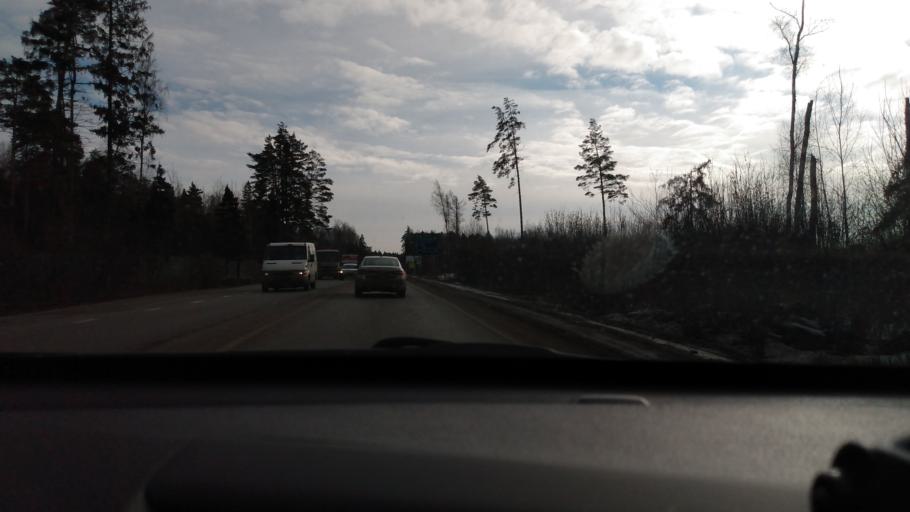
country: RU
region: Moskovskaya
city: Petrovo-Dal'neye
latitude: 55.7862
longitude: 37.1571
